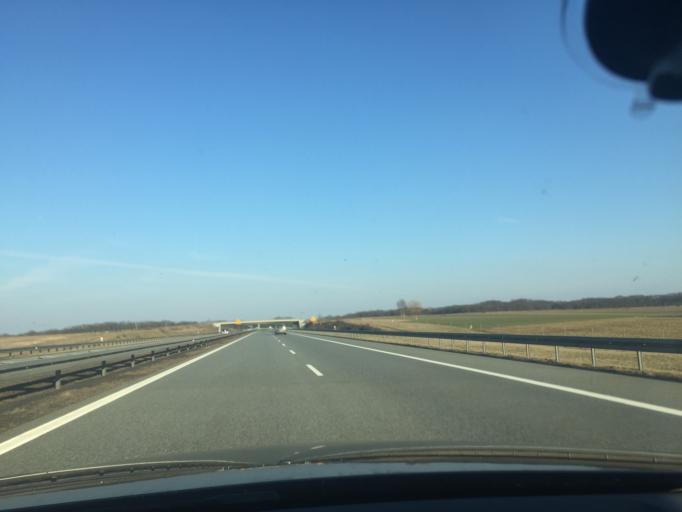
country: PL
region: Greater Poland Voivodeship
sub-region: Powiat nowotomyski
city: Lwowek
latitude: 52.3734
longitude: 16.2268
